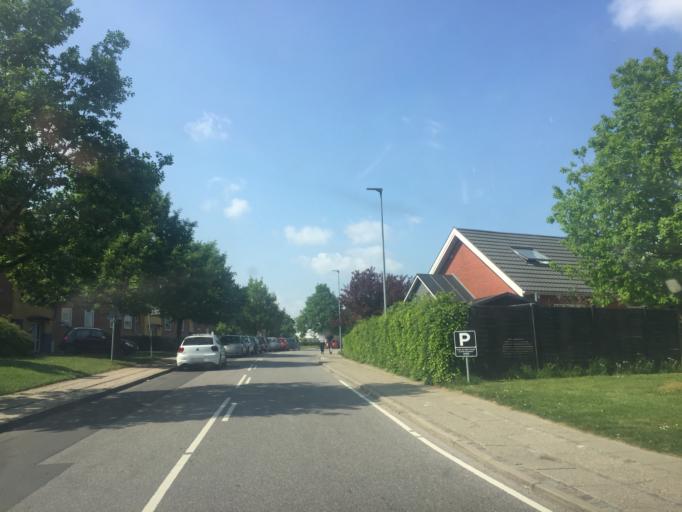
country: DK
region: South Denmark
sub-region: Kolding Kommune
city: Kolding
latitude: 55.4770
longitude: 9.4848
